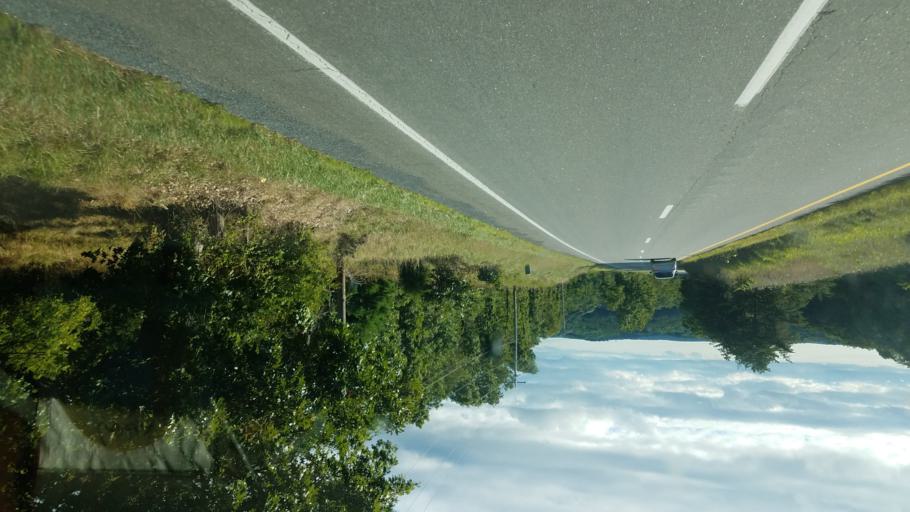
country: US
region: Virginia
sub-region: Frederick County
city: Shawnee Land
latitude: 39.3083
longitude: -78.2882
